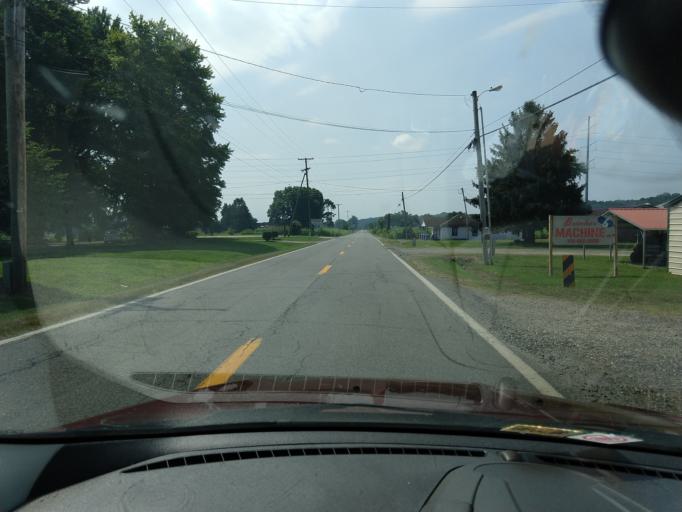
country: US
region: West Virginia
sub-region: Mason County
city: New Haven
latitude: 38.9520
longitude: -81.9218
